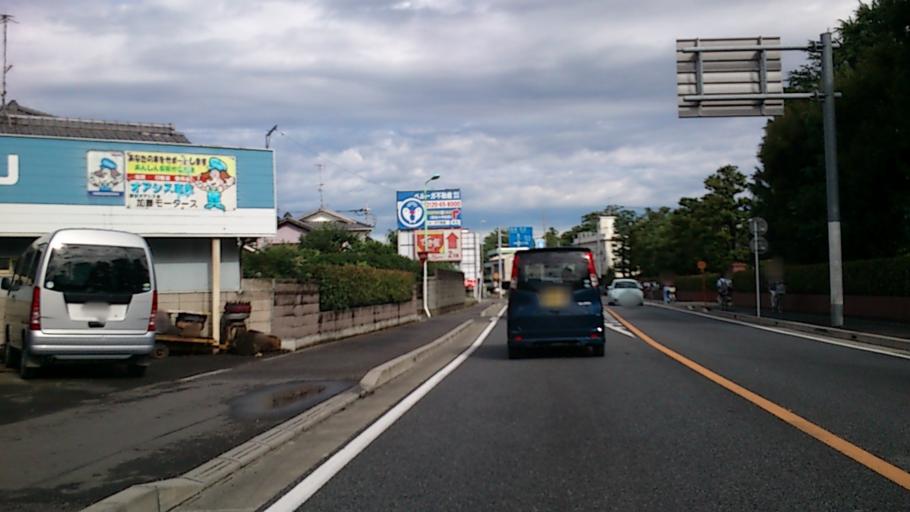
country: JP
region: Saitama
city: Fukayacho
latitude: 36.1963
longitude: 139.2919
